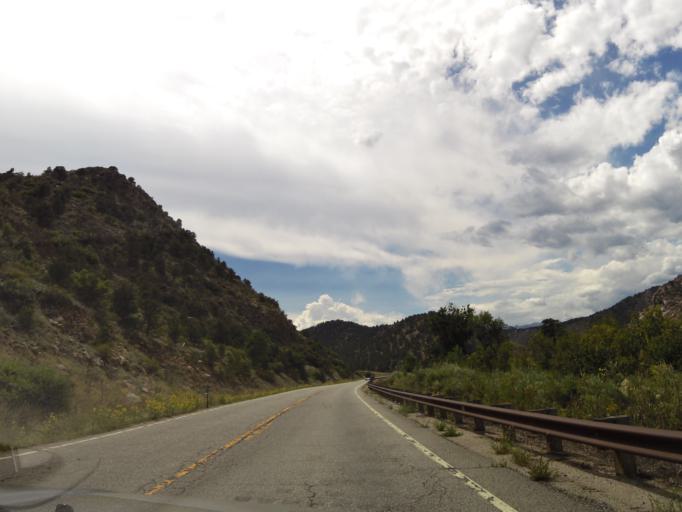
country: US
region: Colorado
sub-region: Custer County
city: Westcliffe
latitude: 38.3922
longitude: -105.6394
